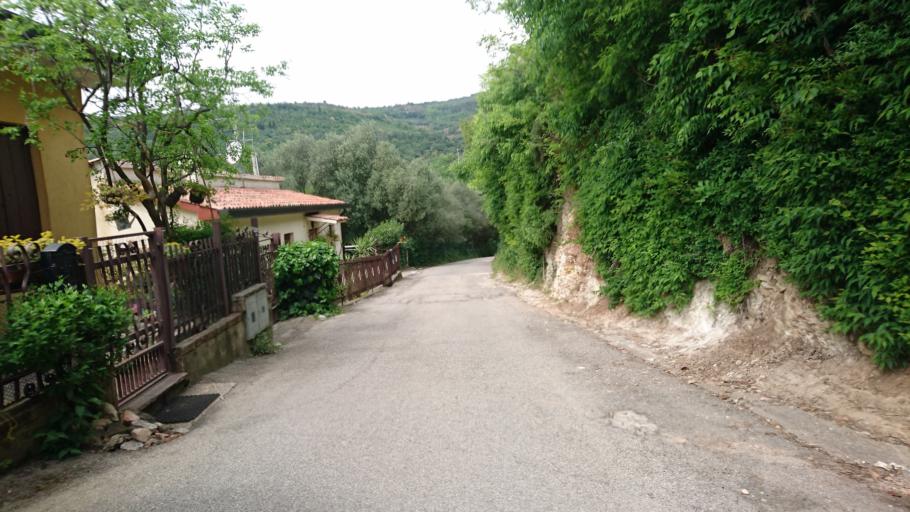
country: IT
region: Veneto
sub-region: Provincia di Padova
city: Arqua Petrarca
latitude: 45.2710
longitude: 11.7150
